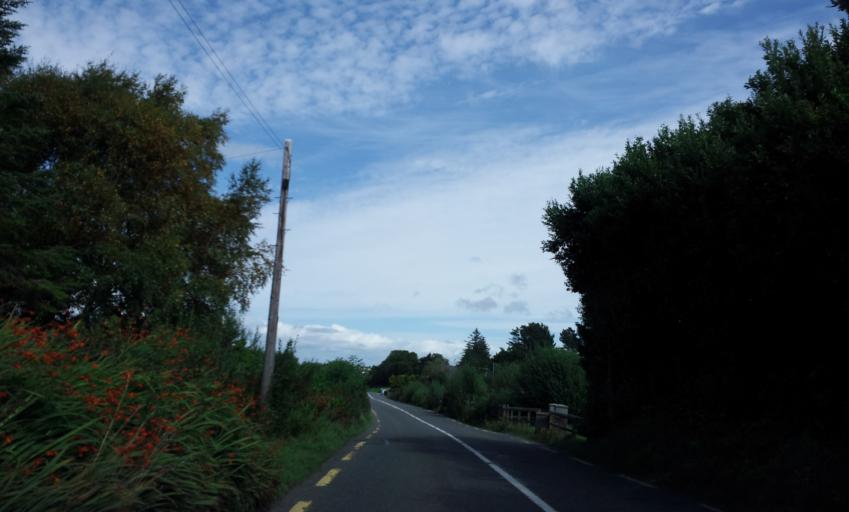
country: IE
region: Munster
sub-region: Ciarrai
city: Killorglin
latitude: 52.0616
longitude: -9.9172
